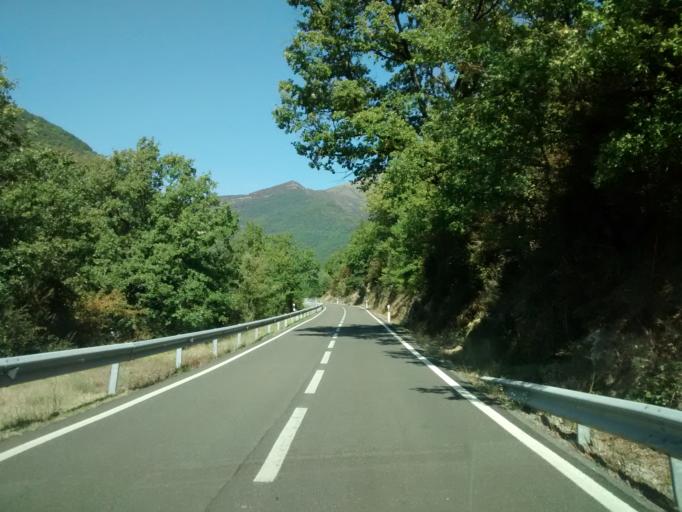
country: ES
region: Aragon
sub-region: Provincia de Huesca
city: Fiscal
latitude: 42.5191
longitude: -0.1290
